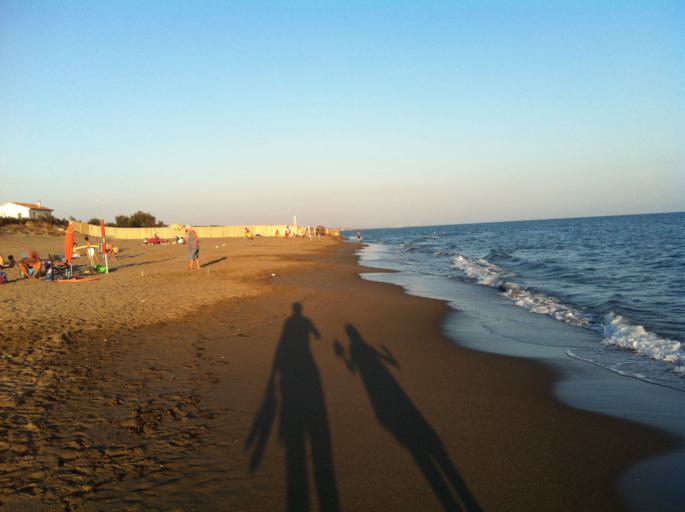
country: IT
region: Latium
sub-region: Provincia di Viterbo
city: Pescia Romana
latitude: 42.3785
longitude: 11.4464
